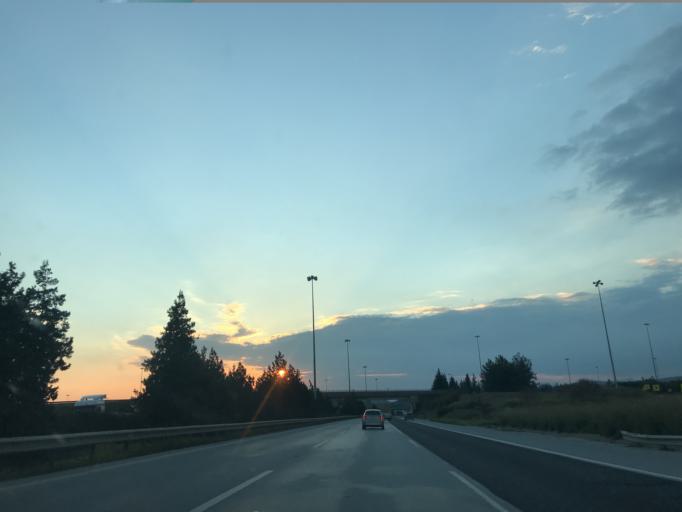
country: TR
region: Mersin
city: Yenice
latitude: 37.0082
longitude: 34.9713
